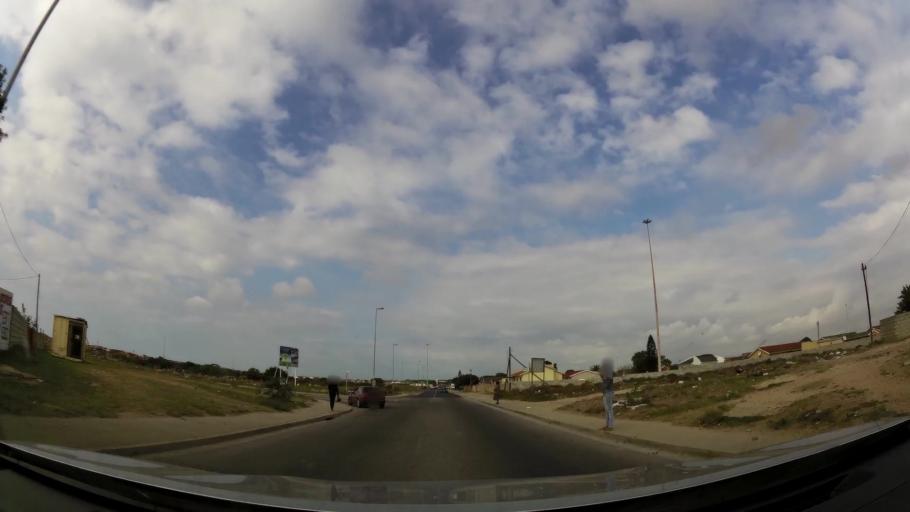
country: ZA
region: Eastern Cape
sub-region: Nelson Mandela Bay Metropolitan Municipality
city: Port Elizabeth
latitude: -33.8220
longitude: 25.5904
